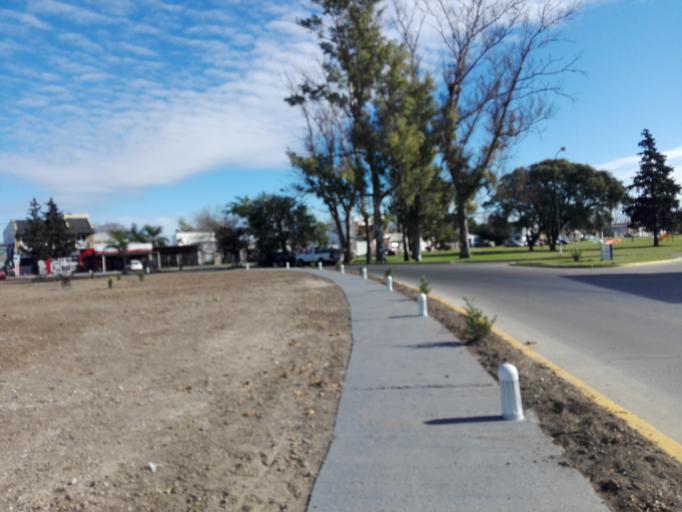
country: AR
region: Buenos Aires
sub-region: Partido de La Plata
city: La Plata
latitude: -34.9533
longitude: -57.9525
